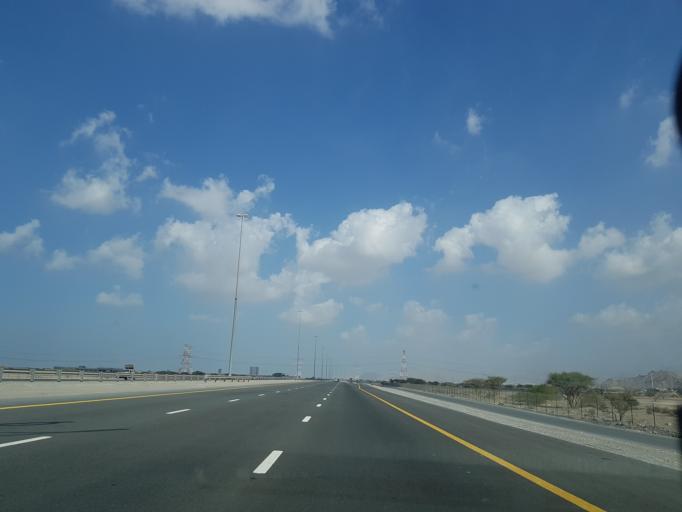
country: AE
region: Ra's al Khaymah
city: Ras al-Khaimah
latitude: 25.7410
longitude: 56.0159
